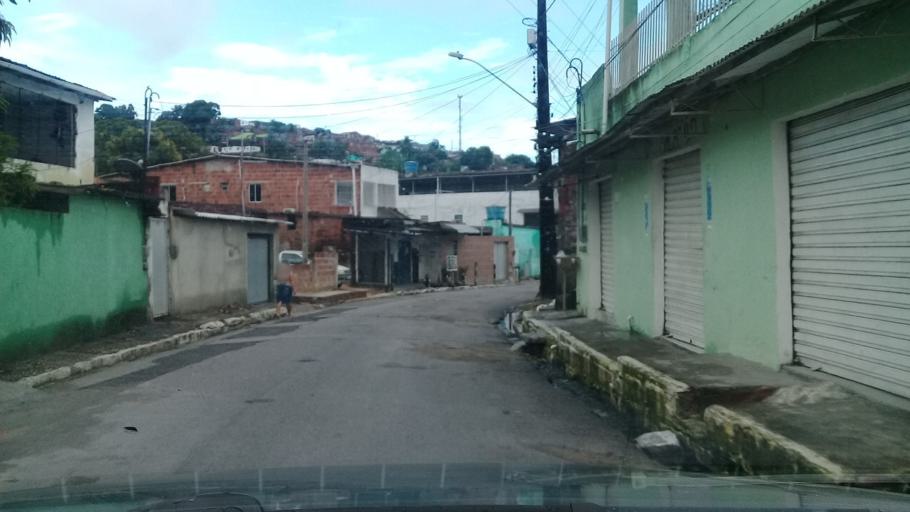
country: BR
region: Pernambuco
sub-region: Jaboatao Dos Guararapes
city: Jaboatao dos Guararapes
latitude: -8.1281
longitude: -34.9487
